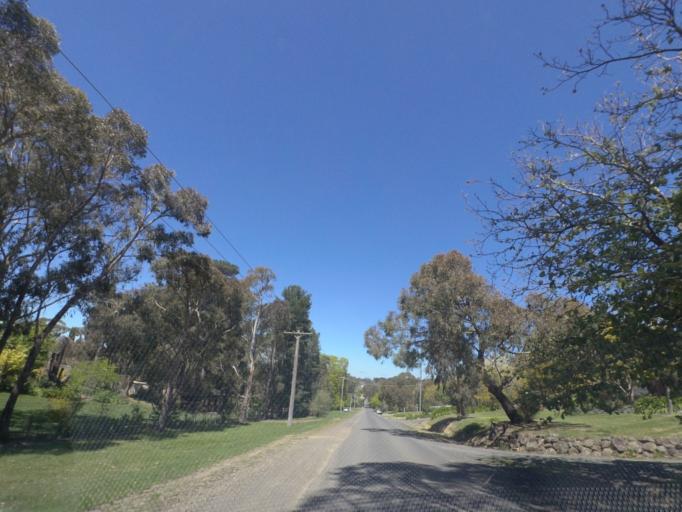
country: AU
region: Victoria
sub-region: Hume
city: Sunbury
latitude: -37.4125
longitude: 144.5616
